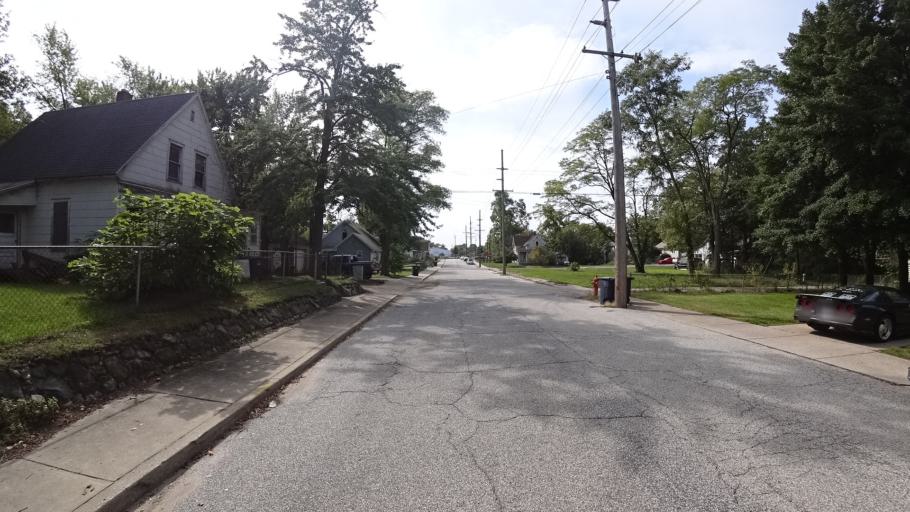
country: US
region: Indiana
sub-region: LaPorte County
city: Michigan City
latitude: 41.7153
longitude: -86.8874
